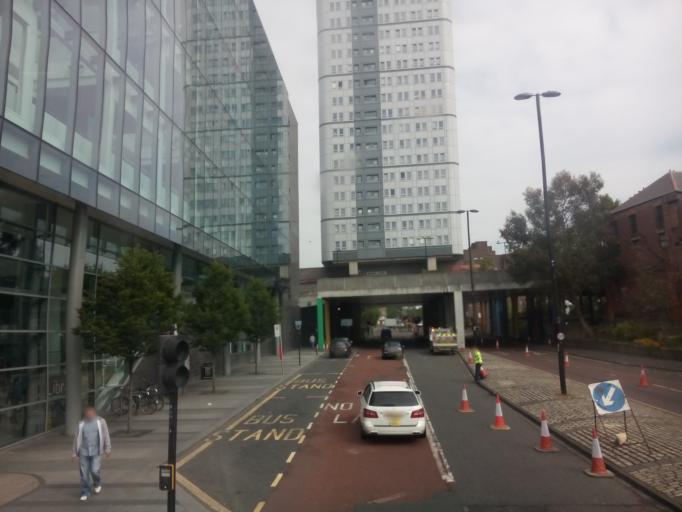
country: GB
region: England
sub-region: Newcastle upon Tyne
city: Newcastle upon Tyne
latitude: 54.9746
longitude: -1.6098
